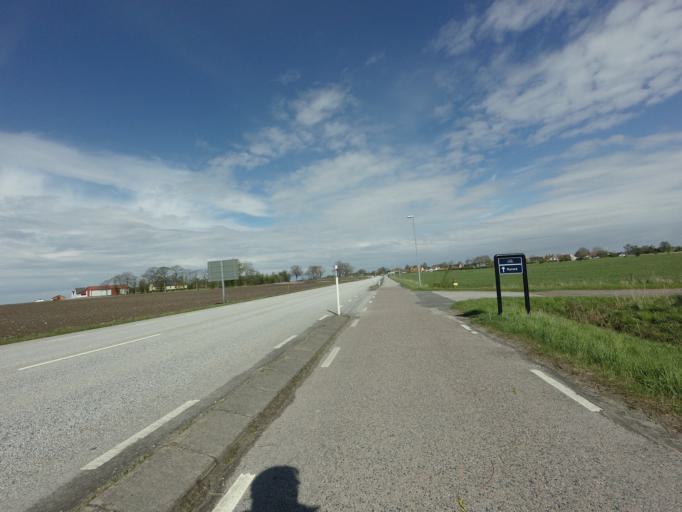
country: SE
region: Skane
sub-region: Vellinge Kommun
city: Vellinge
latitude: 55.4836
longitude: 13.0136
